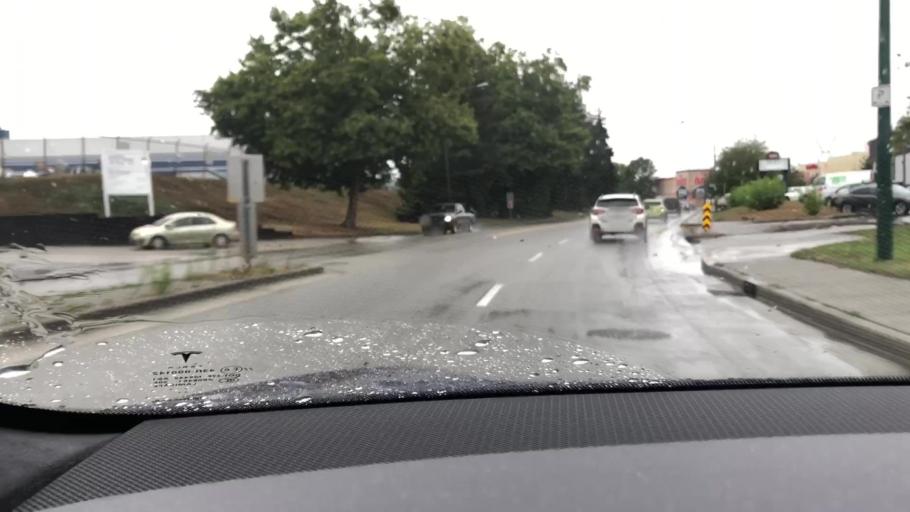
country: CA
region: British Columbia
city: Port Moody
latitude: 49.2299
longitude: -122.8560
